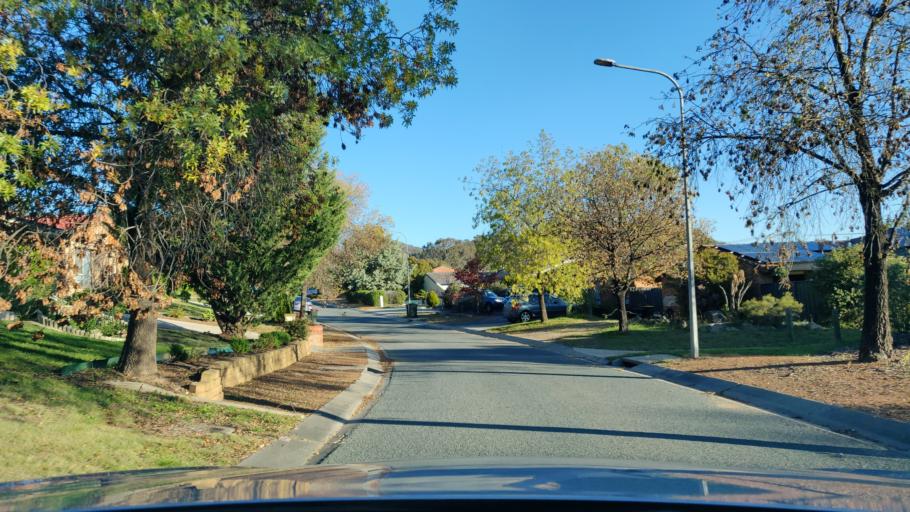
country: AU
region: Australian Capital Territory
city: Macarthur
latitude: -35.4427
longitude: 149.1273
